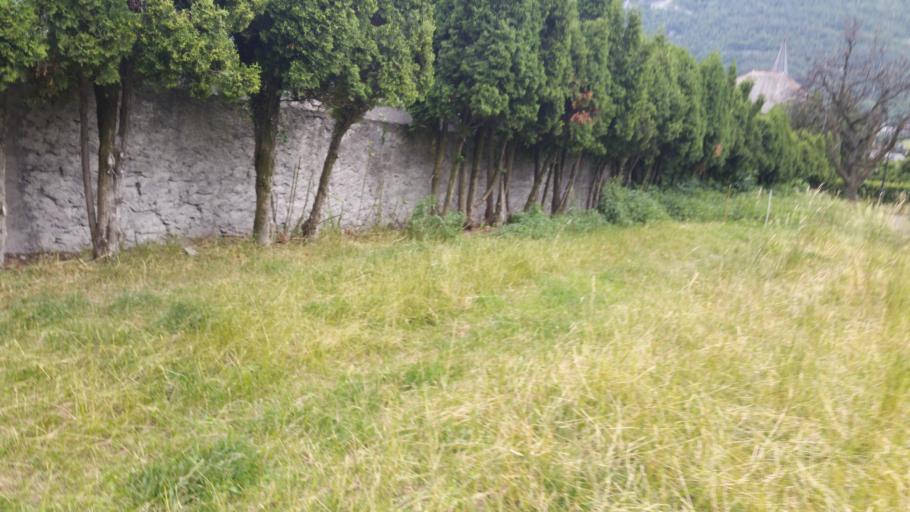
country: FR
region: Rhone-Alpes
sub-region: Departement de la Savoie
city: Villargondran
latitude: 45.2575
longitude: 6.4038
